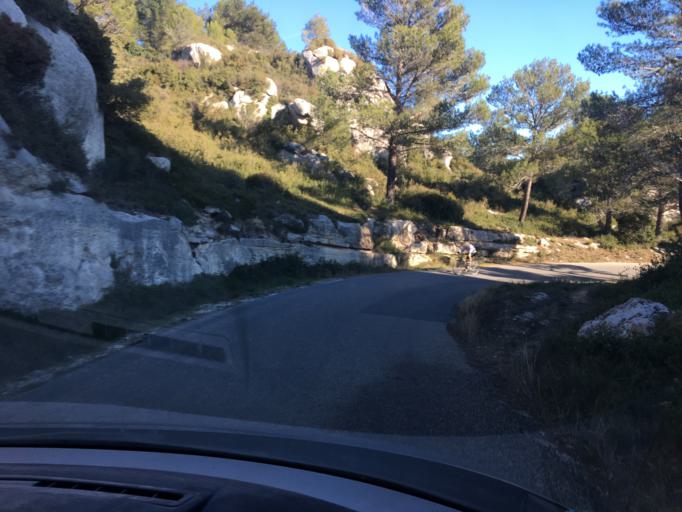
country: FR
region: Provence-Alpes-Cote d'Azur
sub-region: Departement des Bouches-du-Rhone
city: Maussane-les-Alpilles
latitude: 43.7519
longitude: 4.7927
